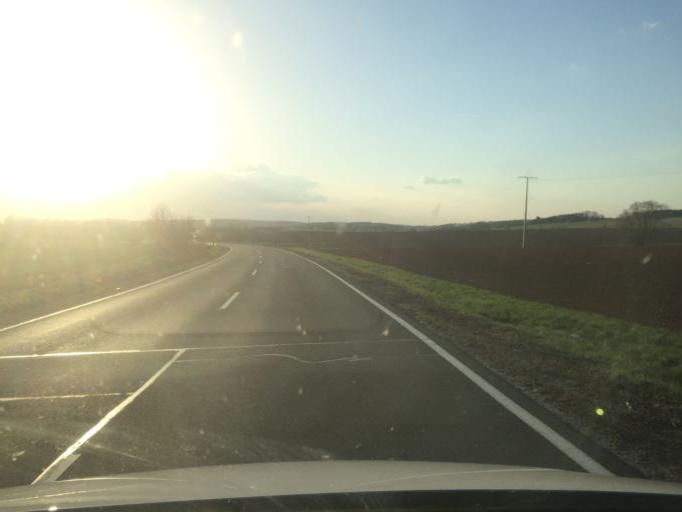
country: DE
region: Lower Saxony
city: Bad Sachsa
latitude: 51.5479
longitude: 10.5758
